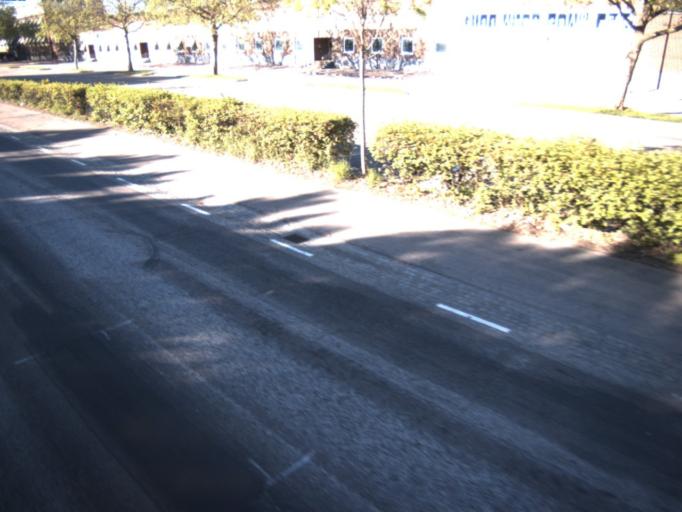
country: SE
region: Skane
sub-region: Helsingborg
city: Helsingborg
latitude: 56.0179
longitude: 12.7287
